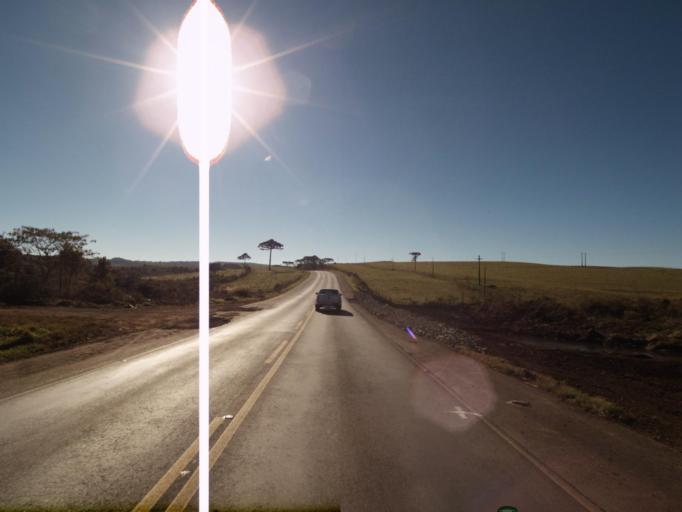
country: BR
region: Santa Catarina
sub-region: Concordia
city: Concordia
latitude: -26.9166
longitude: -51.9231
